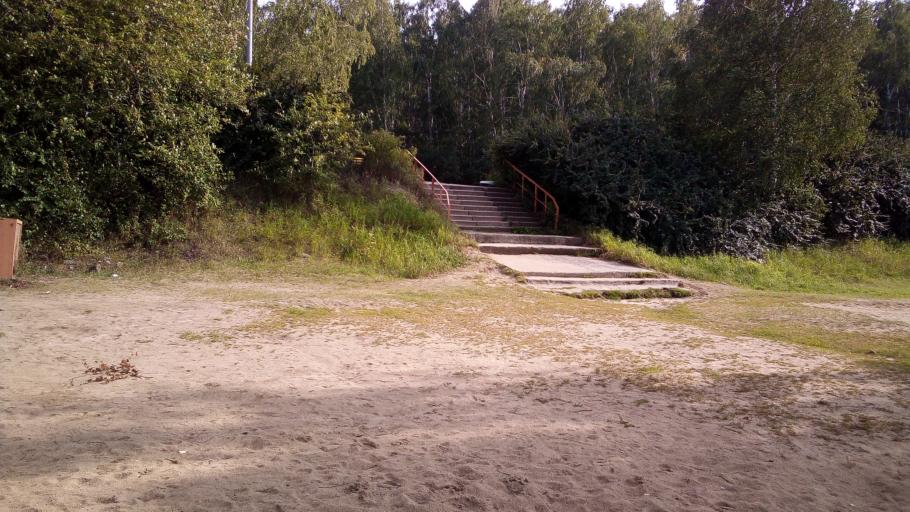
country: RU
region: Chelyabinsk
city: Tayginka
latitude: 55.4777
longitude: 60.4937
